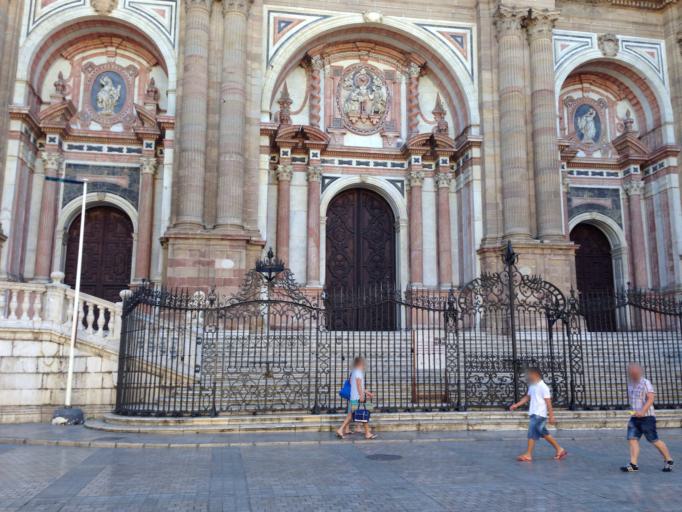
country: ES
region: Andalusia
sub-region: Provincia de Malaga
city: Malaga
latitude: 36.7201
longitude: -4.4203
